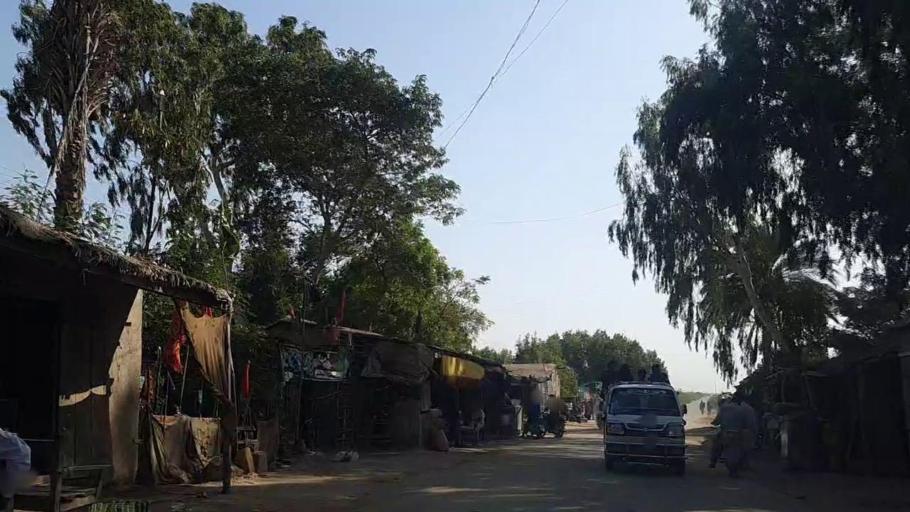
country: PK
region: Sindh
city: Jati
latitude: 24.5138
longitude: 68.2746
